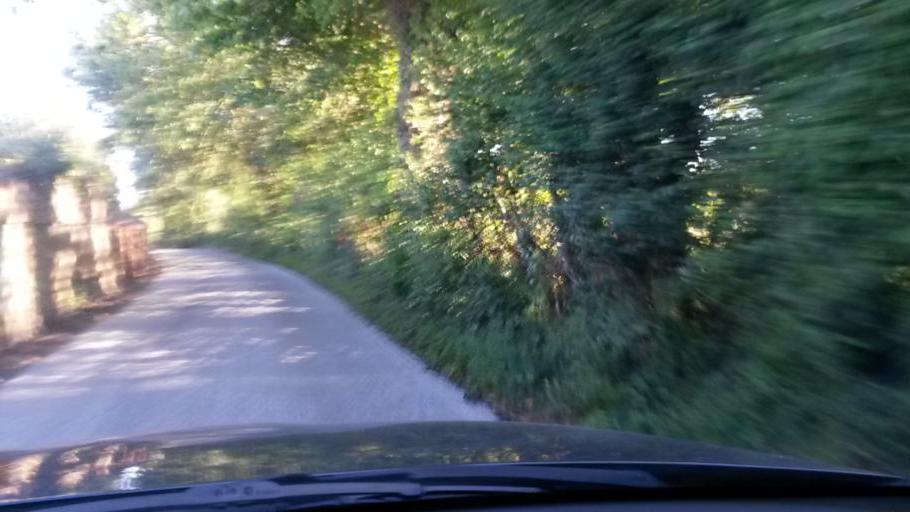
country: IE
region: Leinster
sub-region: Fingal County
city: Swords
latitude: 53.4923
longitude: -6.3058
